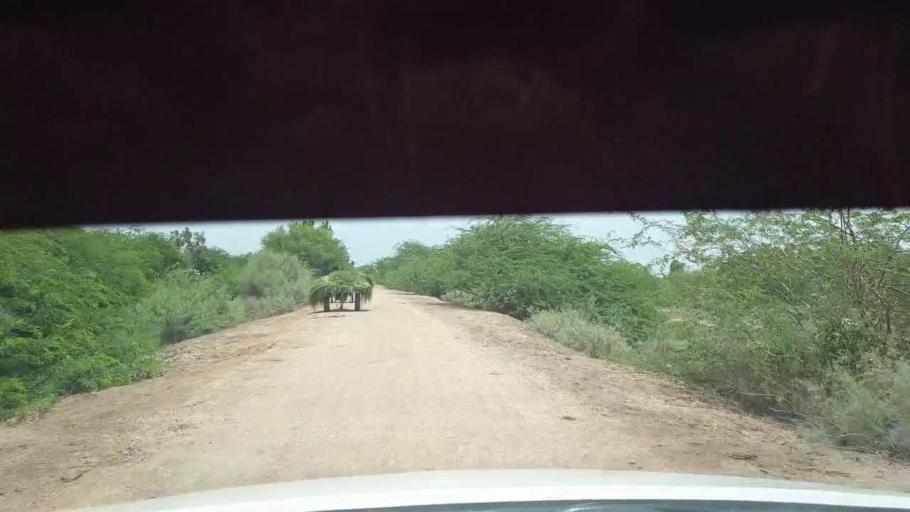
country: PK
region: Sindh
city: Kadhan
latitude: 24.4834
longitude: 69.0028
